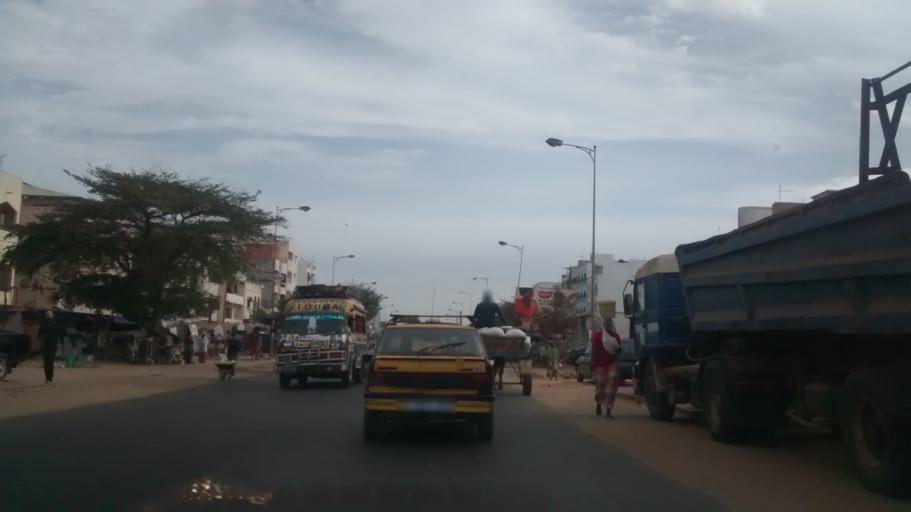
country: SN
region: Dakar
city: Pikine
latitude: 14.7542
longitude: -17.4329
